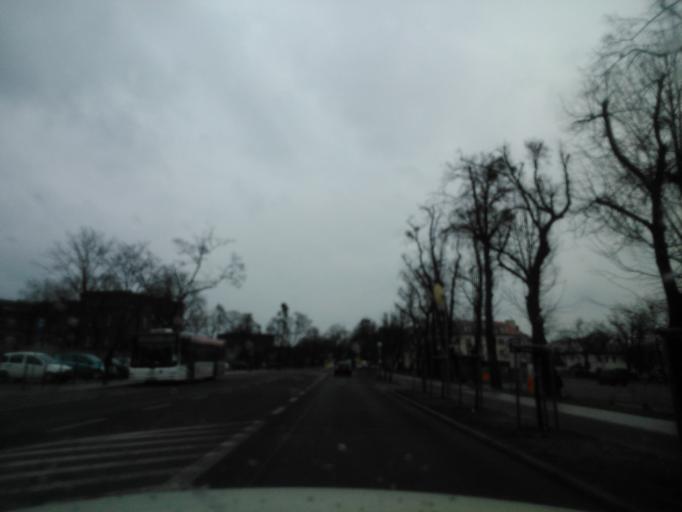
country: PL
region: Kujawsko-Pomorskie
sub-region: Torun
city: Torun
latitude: 53.0138
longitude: 18.6131
